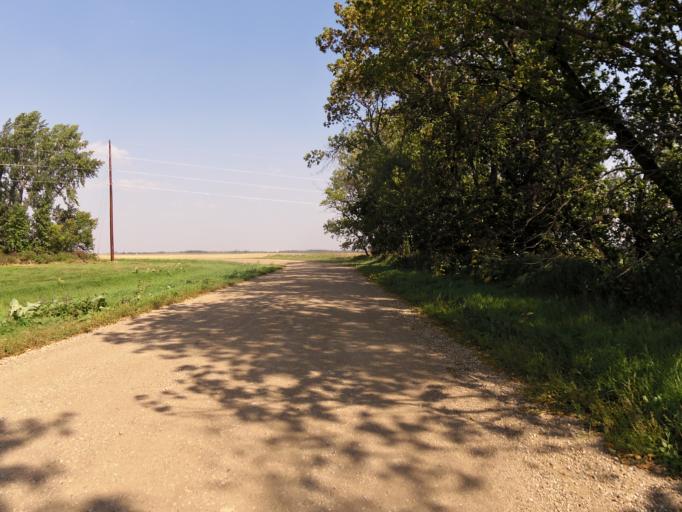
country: US
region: North Dakota
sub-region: Walsh County
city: Grafton
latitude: 48.4281
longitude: -97.3982
